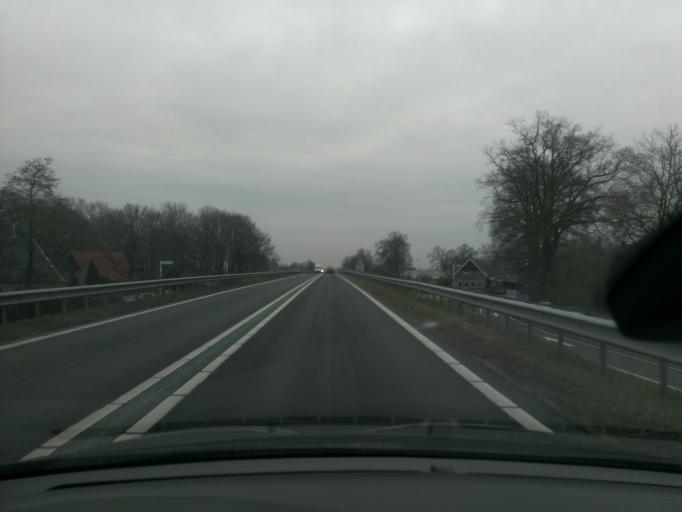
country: NL
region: Overijssel
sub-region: Gemeente Twenterand
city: Vriezenveen
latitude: 52.4162
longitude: 6.6333
